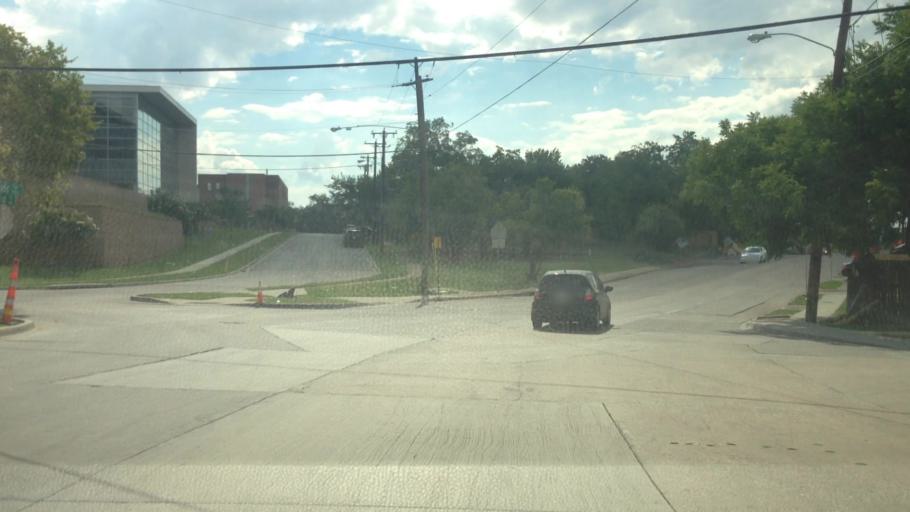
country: US
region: Texas
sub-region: Dallas County
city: Dallas
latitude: 32.7495
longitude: -96.8199
